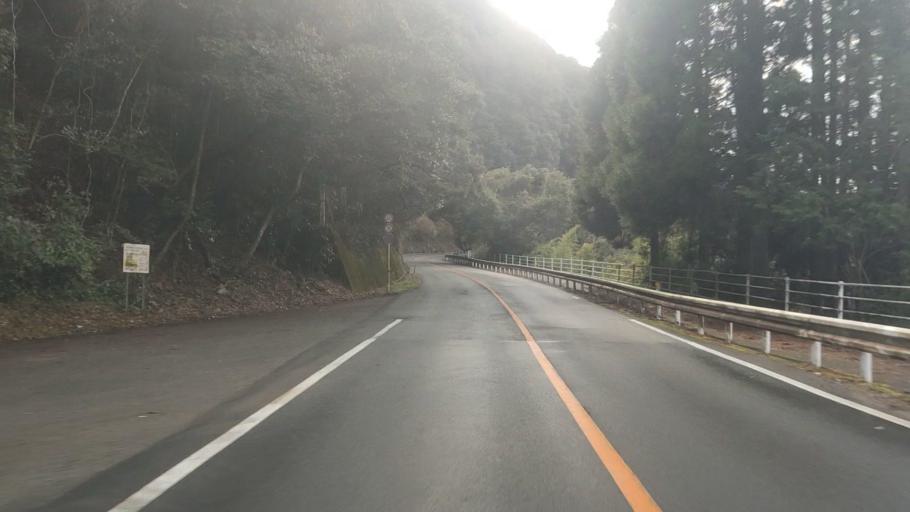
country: JP
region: Kumamoto
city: Hitoyoshi
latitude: 32.3010
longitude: 130.8463
